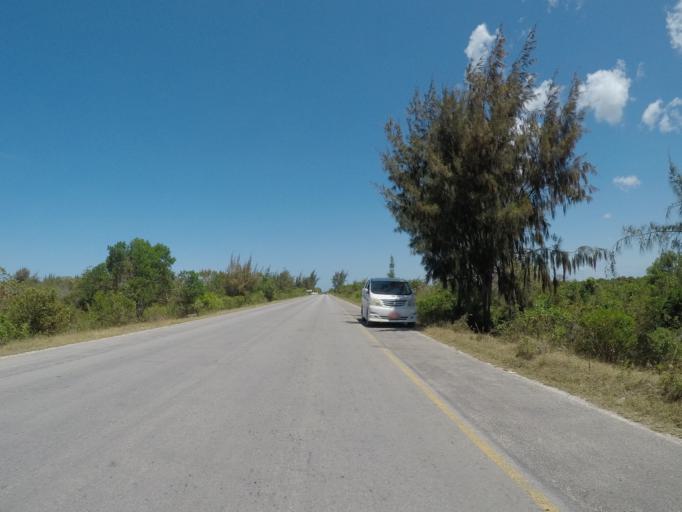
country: TZ
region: Zanzibar Central/South
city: Nganane
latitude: -6.2983
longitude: 39.5381
